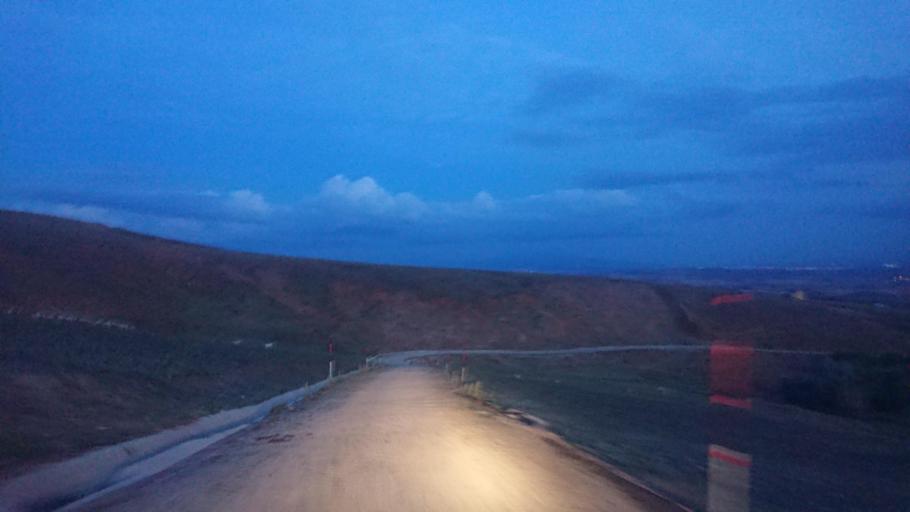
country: TR
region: Aksaray
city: Ortakoy
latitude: 38.6368
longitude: 34.0176
